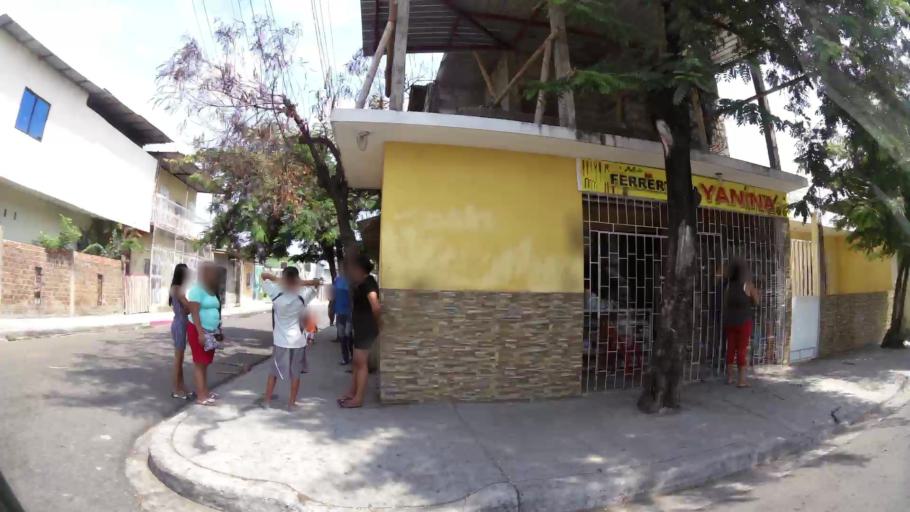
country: EC
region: Guayas
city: Guayaquil
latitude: -2.2648
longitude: -79.8743
